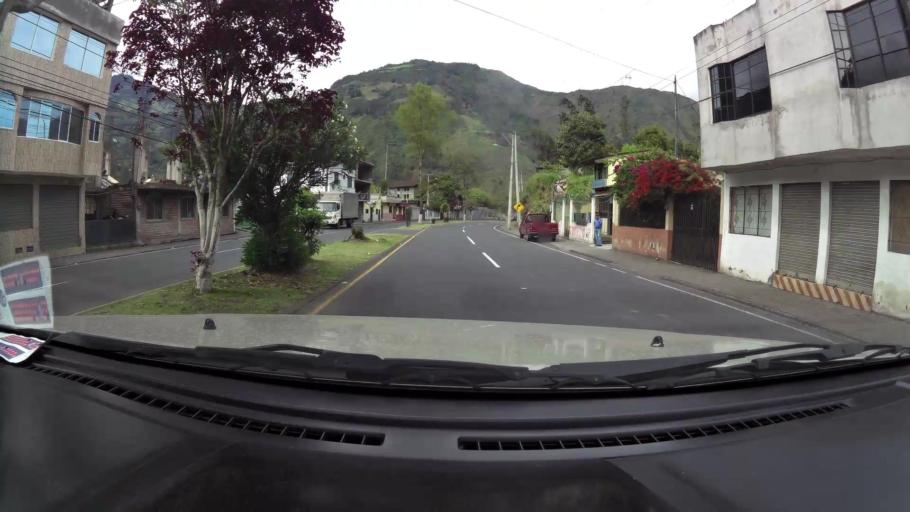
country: EC
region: Tungurahua
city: Banos
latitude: -1.3919
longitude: -78.4203
